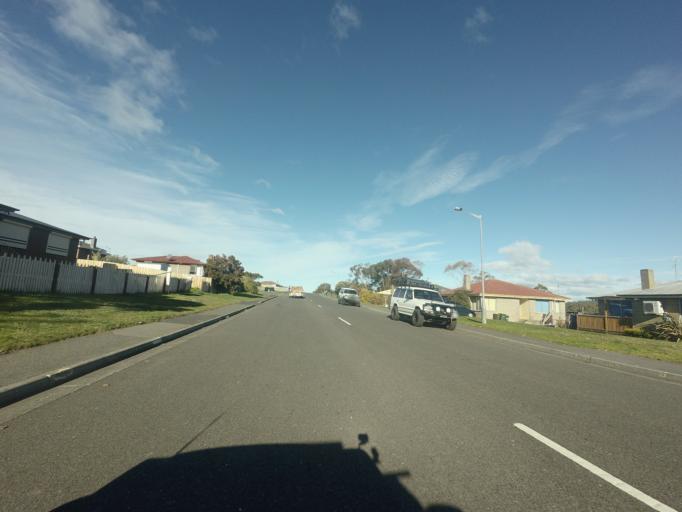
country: AU
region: Tasmania
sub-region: Clarence
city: Rokeby
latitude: -42.8901
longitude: 147.4417
